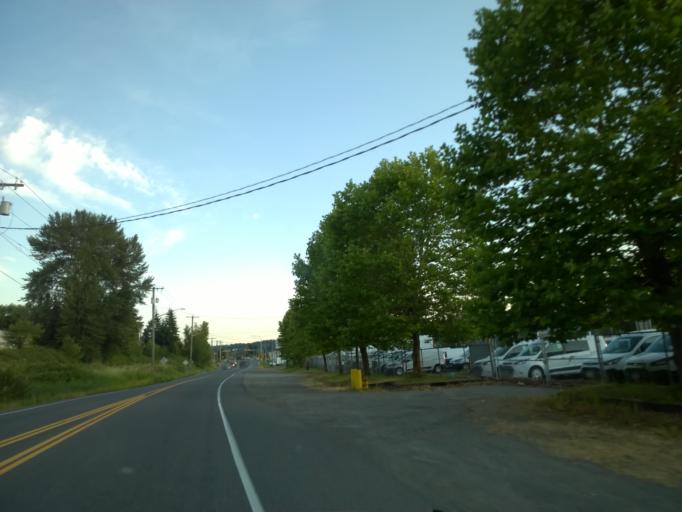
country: US
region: Washington
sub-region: King County
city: Woodinville
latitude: 47.7713
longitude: -122.1539
